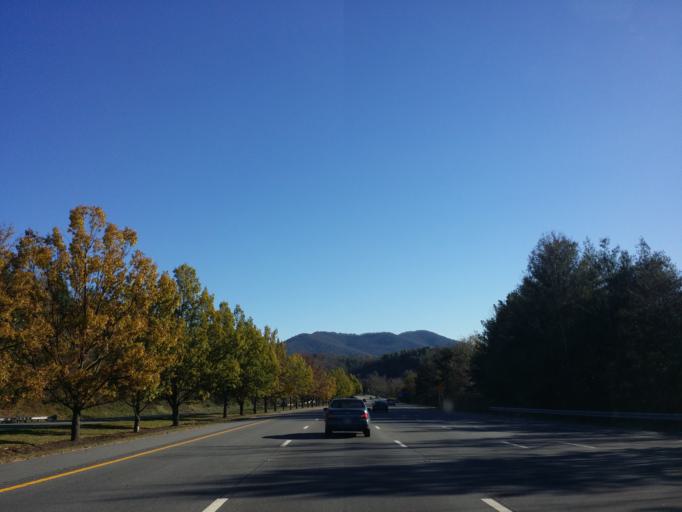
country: US
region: North Carolina
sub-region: Buncombe County
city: Asheville
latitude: 35.5824
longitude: -82.5207
